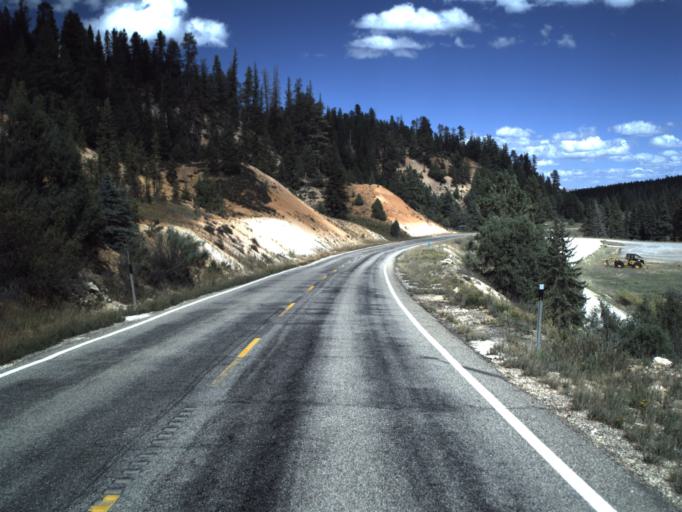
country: US
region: Utah
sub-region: Garfield County
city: Panguitch
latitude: 37.4973
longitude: -112.6040
